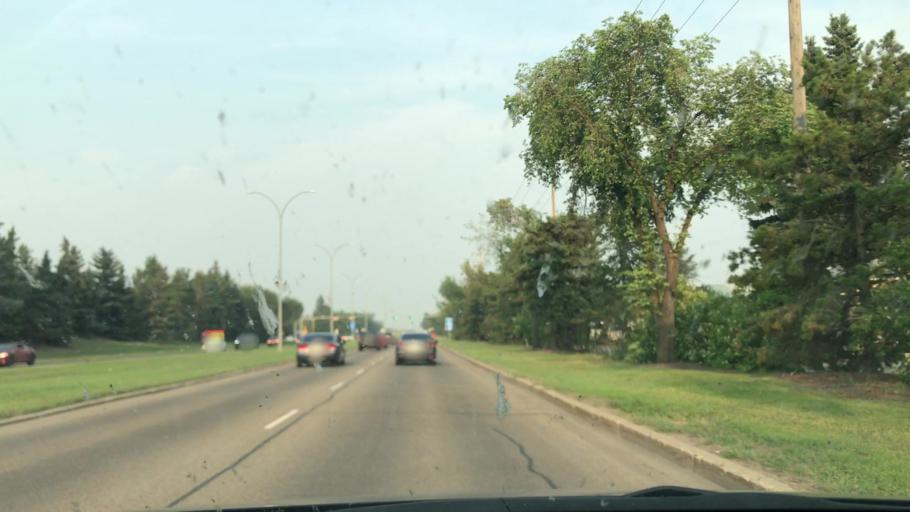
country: CA
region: Alberta
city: Edmonton
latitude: 53.5995
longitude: -113.4591
